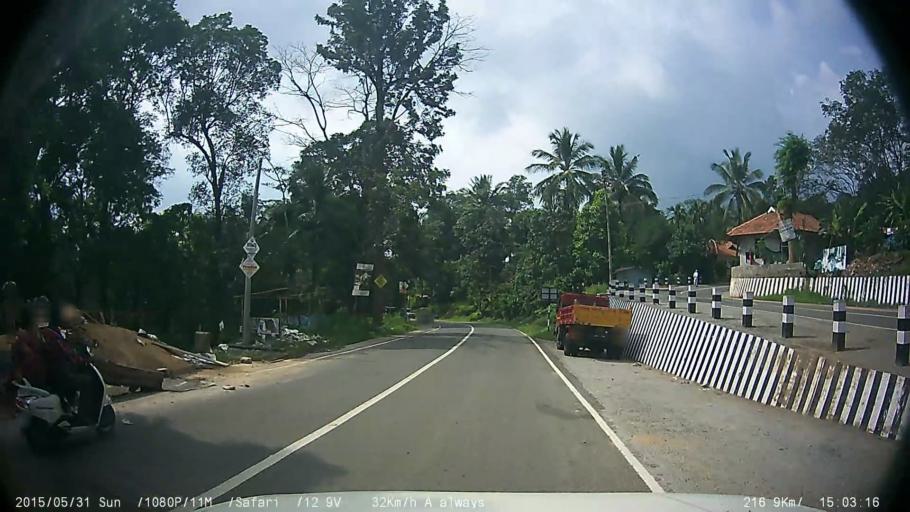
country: IN
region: Kerala
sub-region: Wayanad
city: Kalpetta
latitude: 11.6321
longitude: 76.2152
